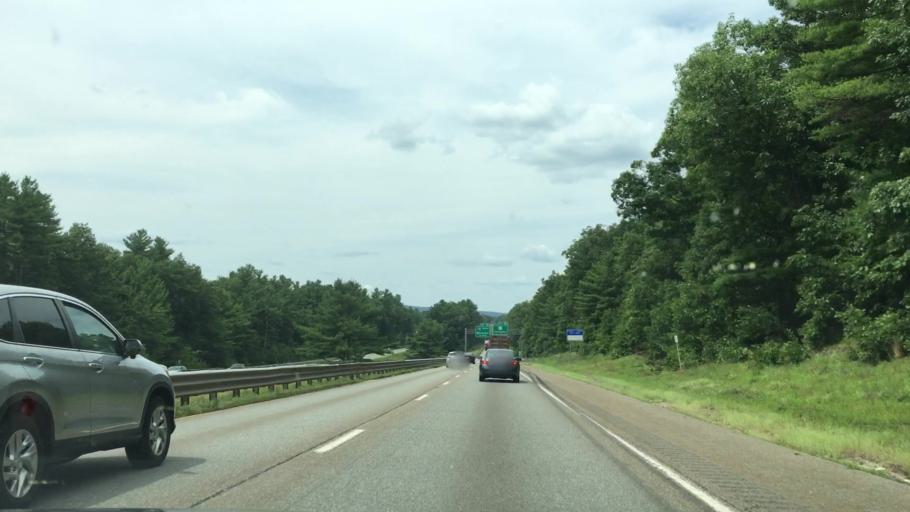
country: US
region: Massachusetts
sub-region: Middlesex County
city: Shirley
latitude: 42.5180
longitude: -71.6785
